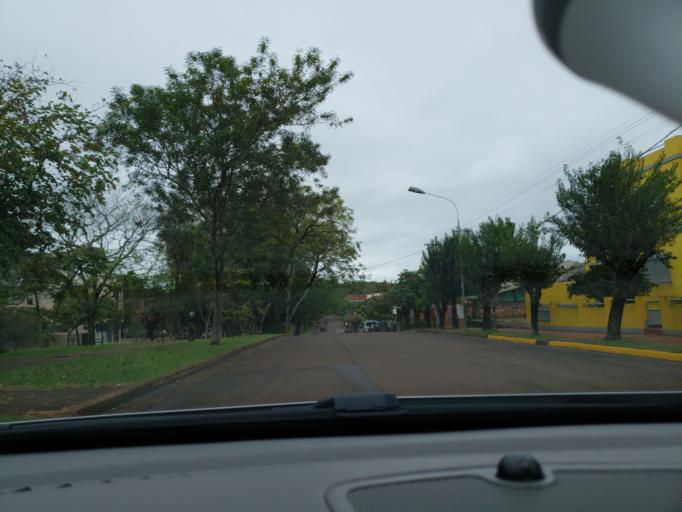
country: AR
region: Misiones
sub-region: Departamento de Apostoles
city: Apostoles
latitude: -27.9116
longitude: -55.7523
